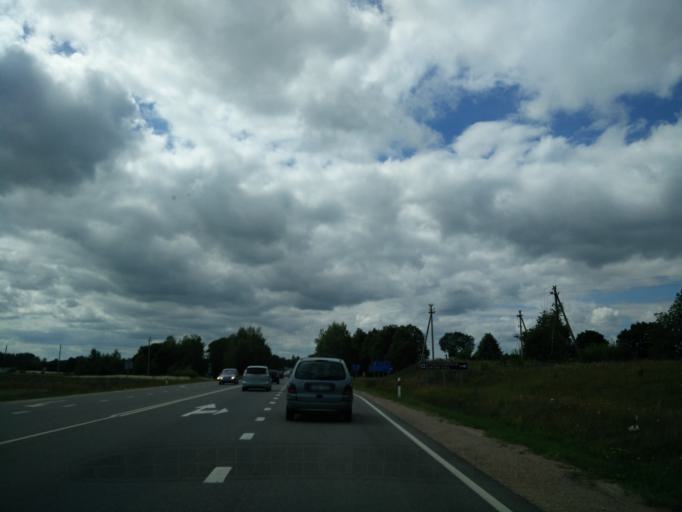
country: LT
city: Trakai
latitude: 54.6272
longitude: 24.9610
